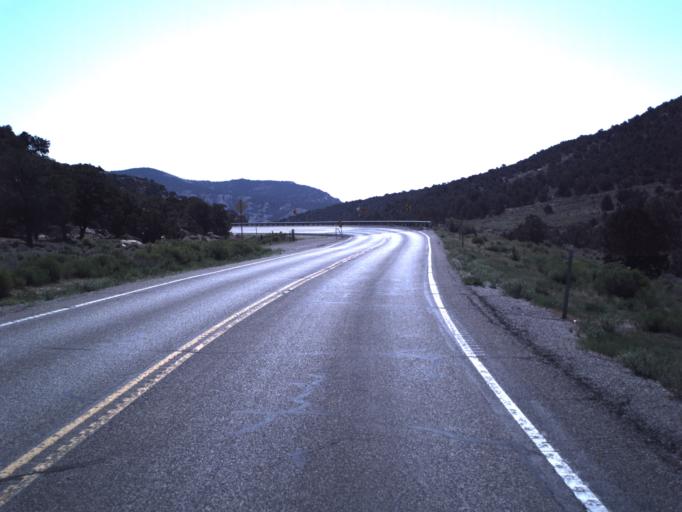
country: US
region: Utah
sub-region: Wayne County
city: Loa
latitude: 38.6723
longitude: -111.4081
